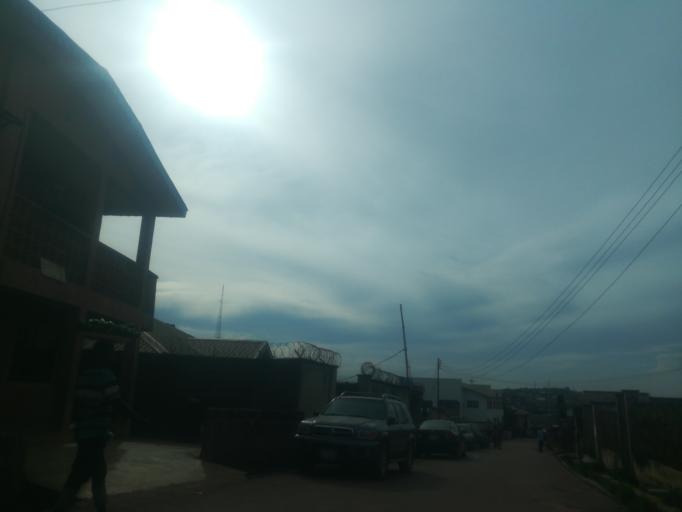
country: NG
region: Oyo
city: Ibadan
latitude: 7.3946
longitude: 3.9402
